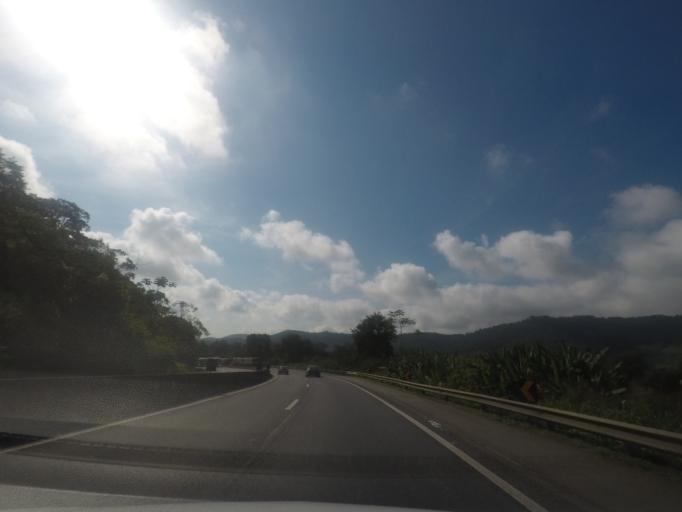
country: BR
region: Parana
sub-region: Antonina
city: Antonina
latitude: -25.5612
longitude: -48.8095
